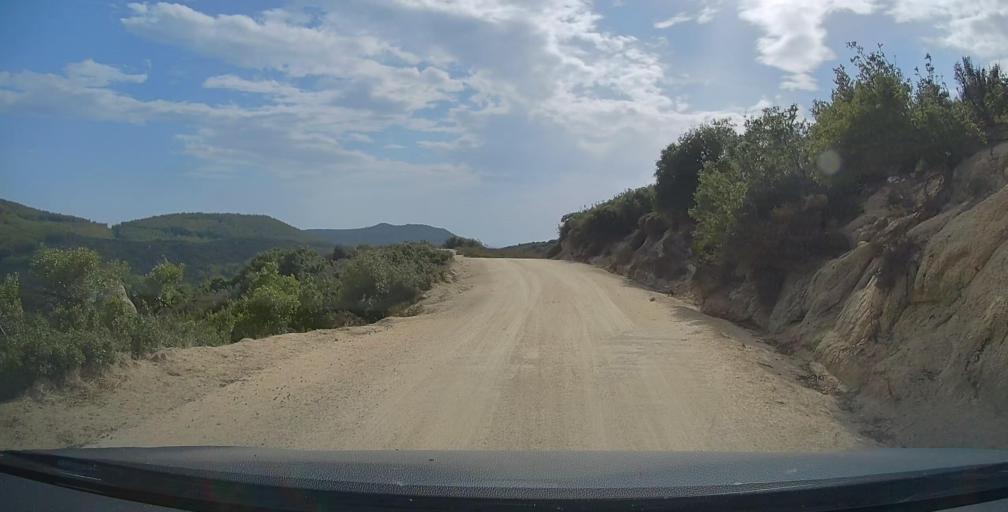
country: GR
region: Central Macedonia
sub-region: Nomos Chalkidikis
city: Sykia
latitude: 39.9963
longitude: 23.9227
